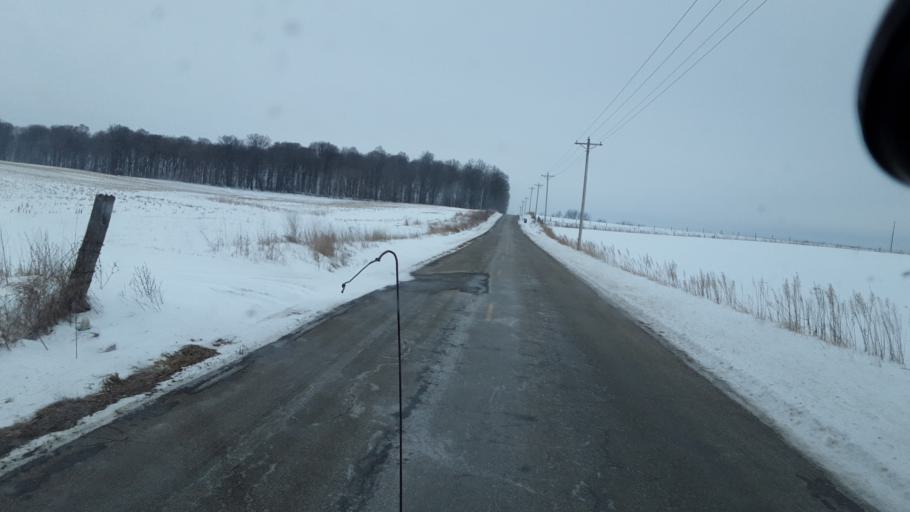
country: US
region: Ohio
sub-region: Knox County
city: Gambier
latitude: 40.3044
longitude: -82.3585
